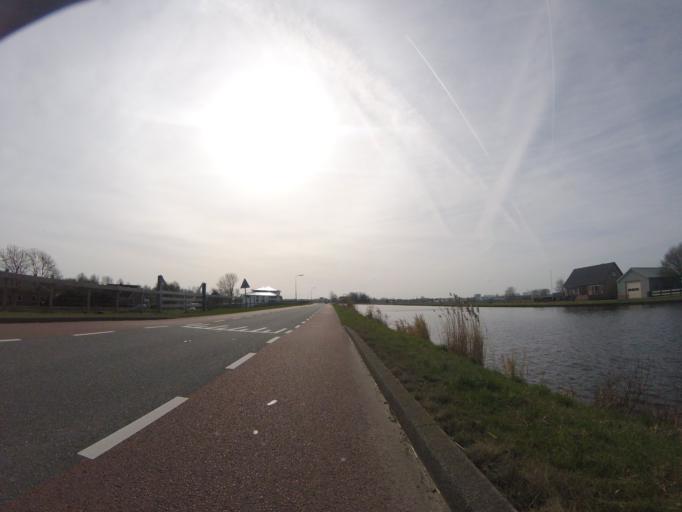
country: NL
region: North Holland
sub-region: Gemeente Bloemendaal
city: Bennebroek
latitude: 52.3067
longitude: 4.6060
